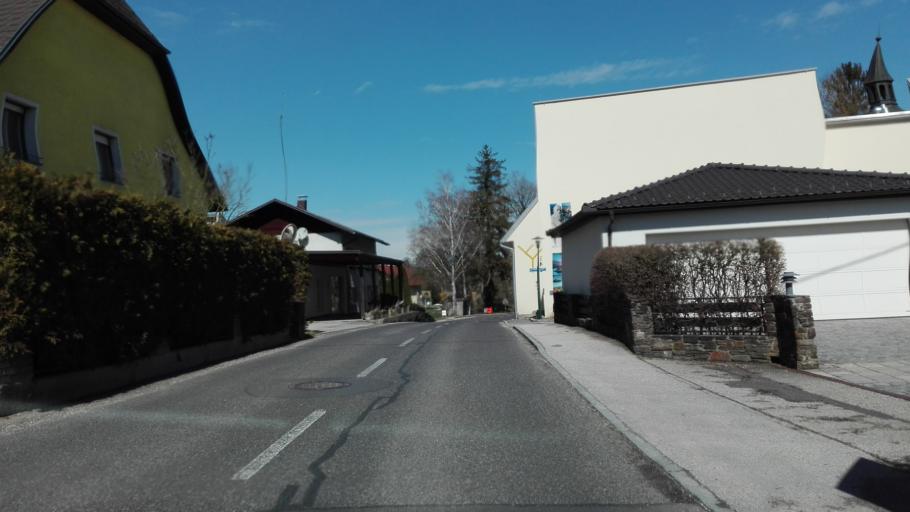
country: AT
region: Upper Austria
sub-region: Politischer Bezirk Grieskirchen
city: Bad Schallerbach
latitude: 48.1940
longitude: 13.9520
